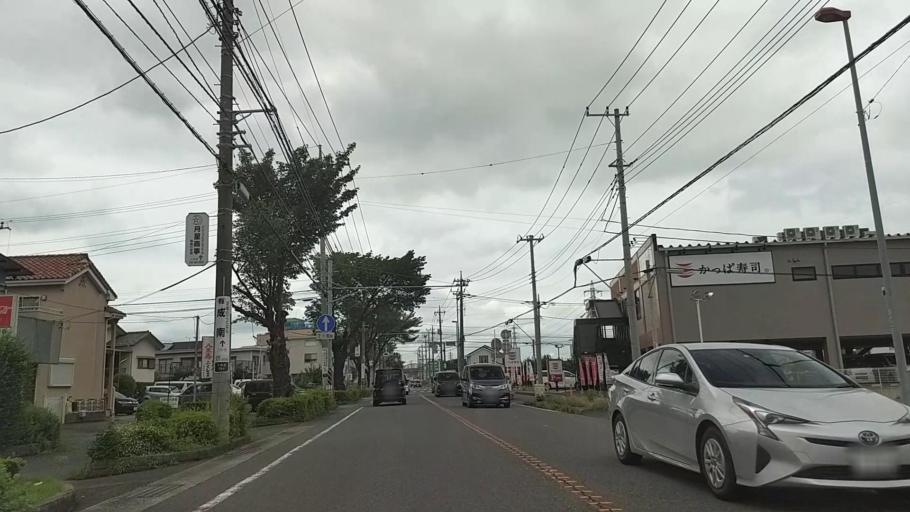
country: JP
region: Kanagawa
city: Minami-rinkan
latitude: 35.4252
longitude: 139.4684
